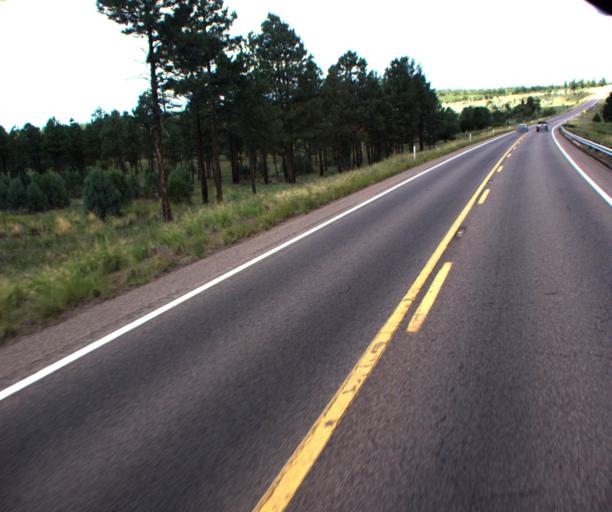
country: US
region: Arizona
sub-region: Navajo County
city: Heber-Overgaard
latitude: 34.3827
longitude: -110.4905
